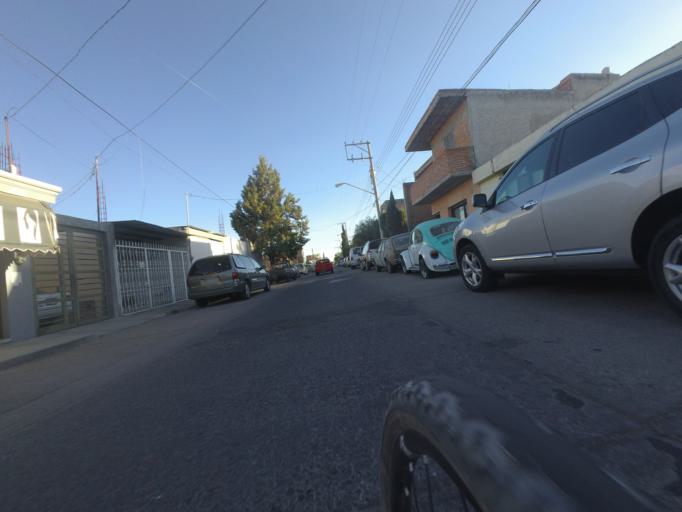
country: MX
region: Aguascalientes
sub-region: Aguascalientes
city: La Loma de los Negritos
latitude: 21.8537
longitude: -102.3420
